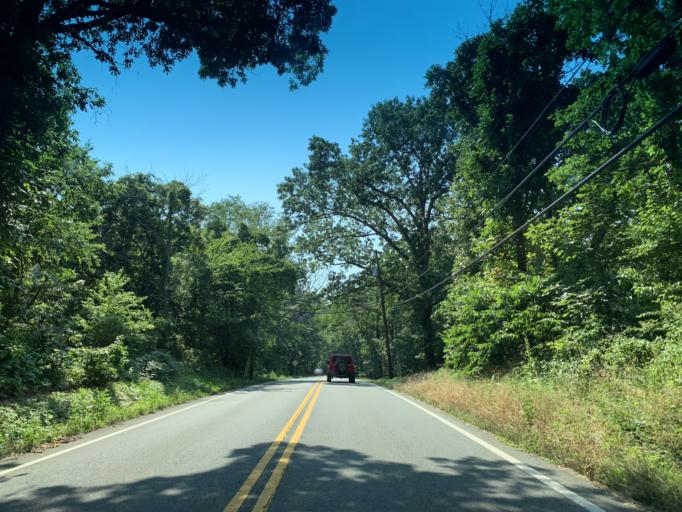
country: US
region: Maryland
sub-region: Montgomery County
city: Poolesville
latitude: 39.1269
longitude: -77.3781
